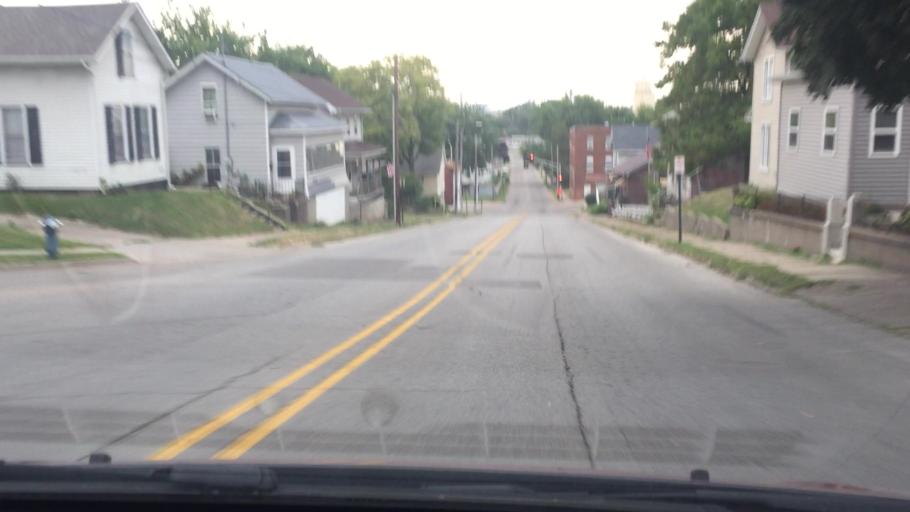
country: US
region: Iowa
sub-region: Muscatine County
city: Muscatine
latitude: 41.4166
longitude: -91.0589
